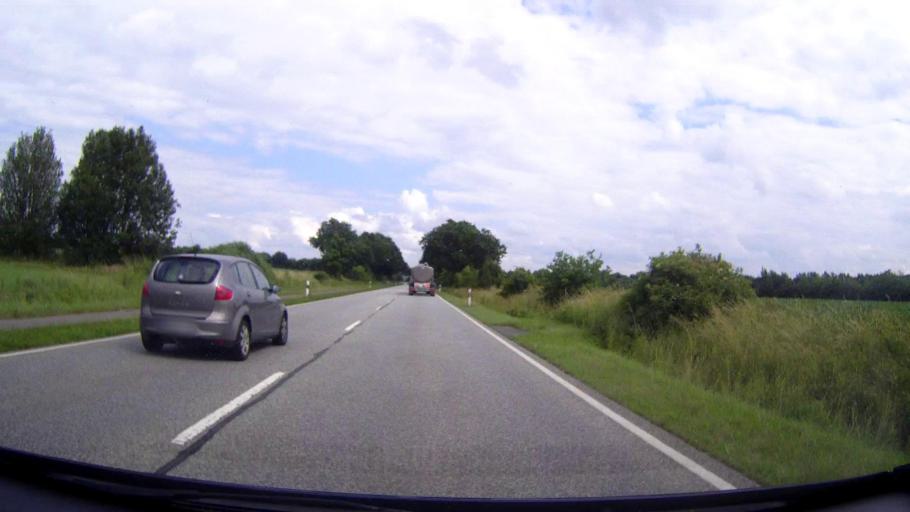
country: DE
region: Schleswig-Holstein
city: Wasbek
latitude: 54.0707
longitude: 9.8761
